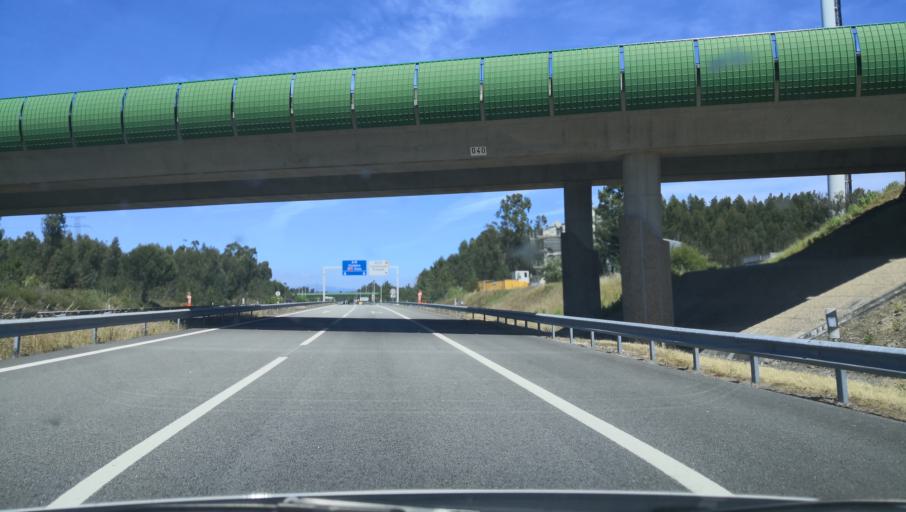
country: PT
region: Coimbra
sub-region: Montemor-O-Velho
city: Arazede
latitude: 40.2570
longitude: -8.6345
